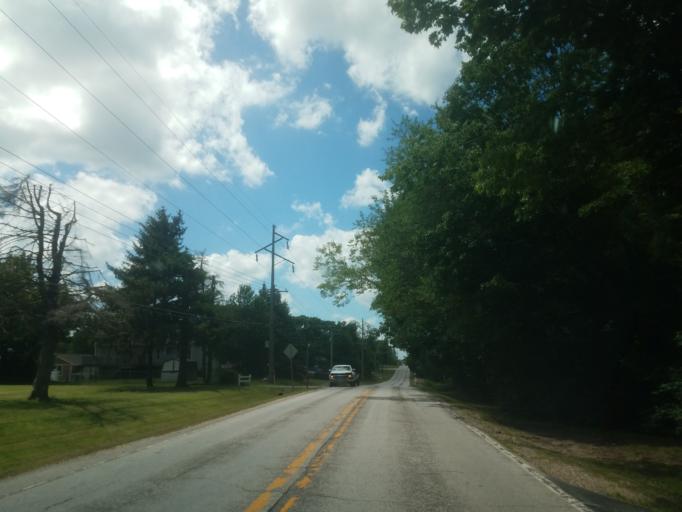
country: US
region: Illinois
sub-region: McLean County
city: Bloomington
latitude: 40.4589
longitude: -89.0147
